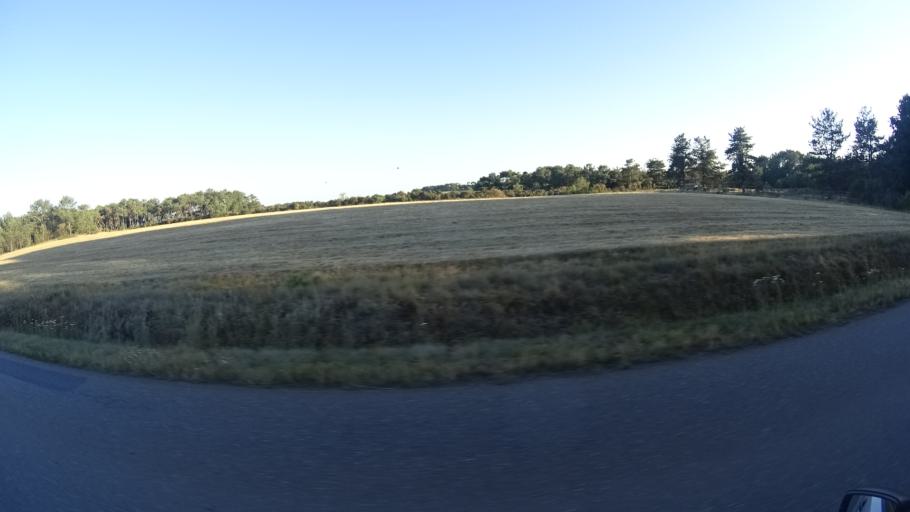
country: FR
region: Brittany
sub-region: Departement d'Ille-et-Vilaine
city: Langon
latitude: 47.7184
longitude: -1.8807
